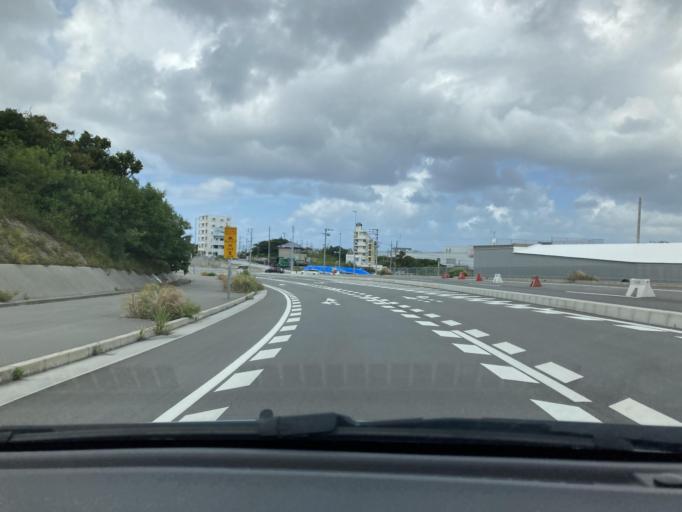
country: JP
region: Okinawa
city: Ginowan
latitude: 26.2681
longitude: 127.7098
